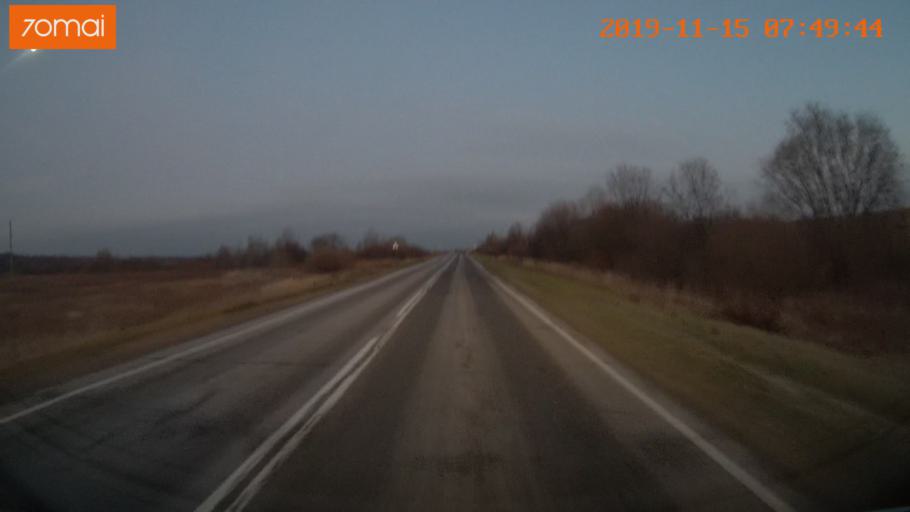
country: RU
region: Vologda
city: Cherepovets
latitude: 58.8616
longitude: 38.2292
